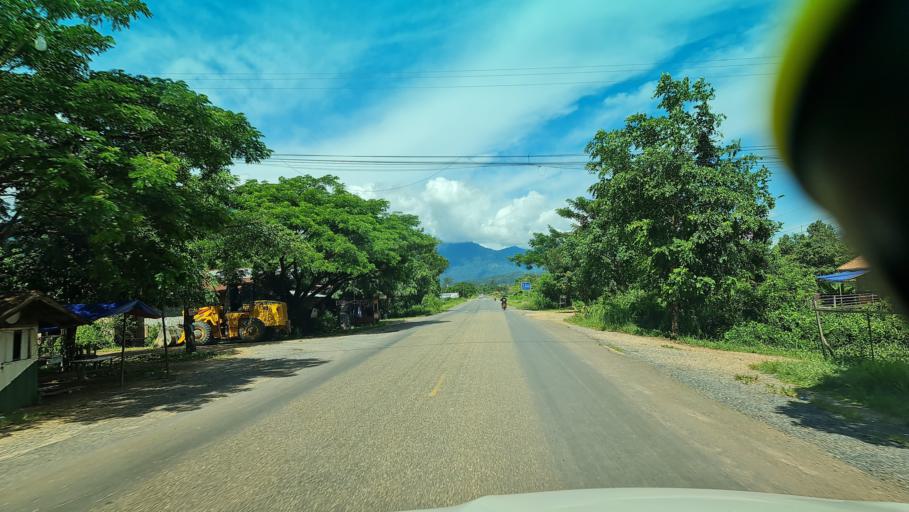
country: LA
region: Bolikhamxai
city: Ban Nahin
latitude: 18.3005
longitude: 104.1165
